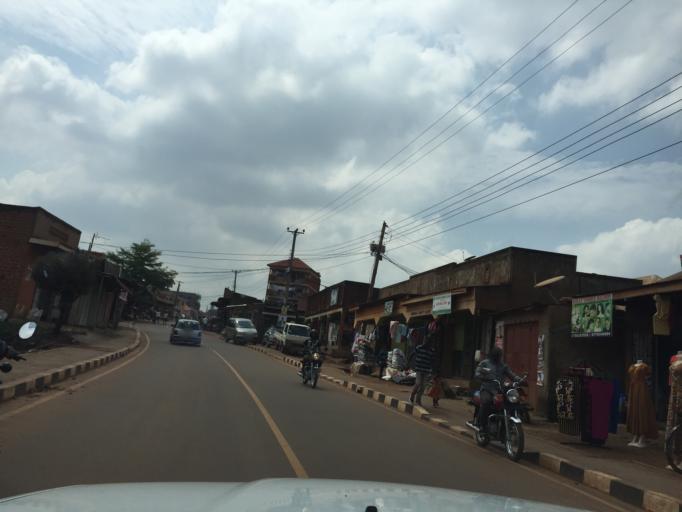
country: UG
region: Central Region
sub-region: Kampala District
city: Kampala
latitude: 0.2873
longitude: 32.5966
